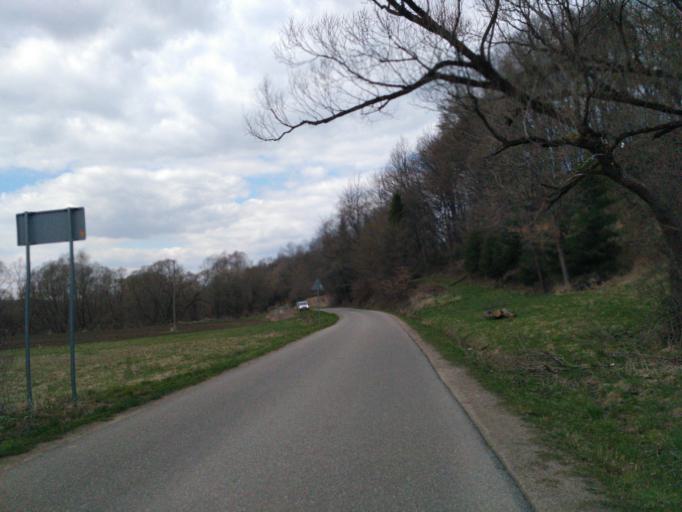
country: PL
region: Subcarpathian Voivodeship
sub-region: Powiat sanocki
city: Tyrawa Woloska
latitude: 49.6597
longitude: 22.3005
